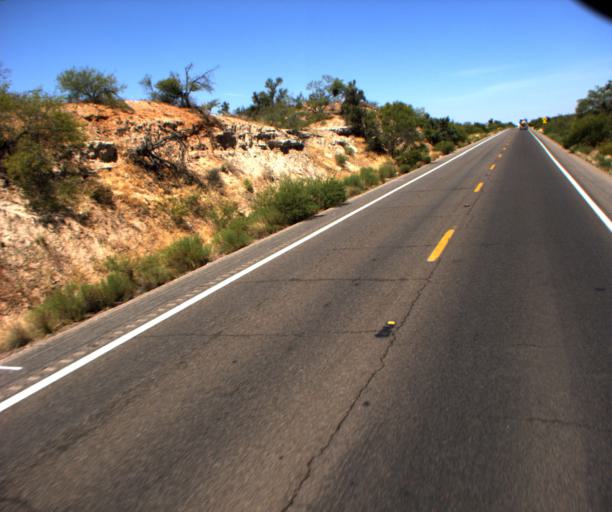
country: US
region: Arizona
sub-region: Gila County
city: Peridot
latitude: 33.3058
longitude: -110.4872
